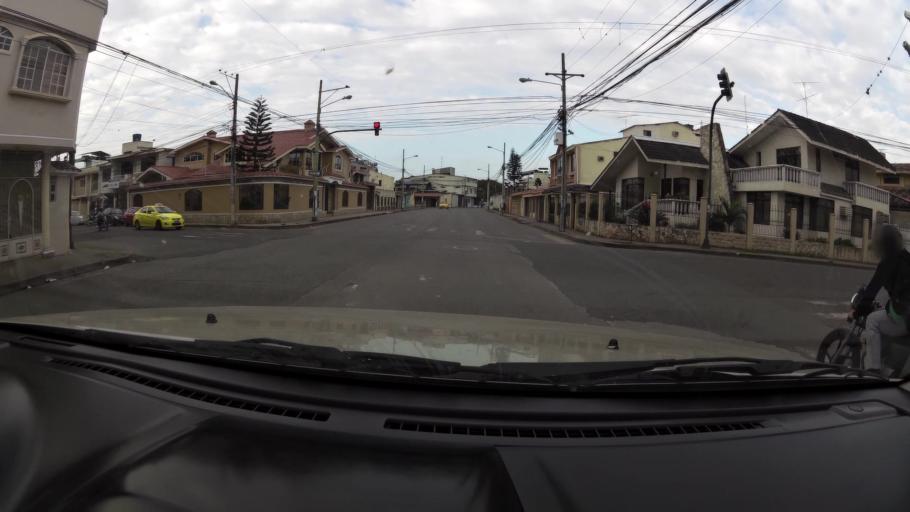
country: EC
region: El Oro
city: Machala
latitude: -3.2635
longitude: -79.9476
